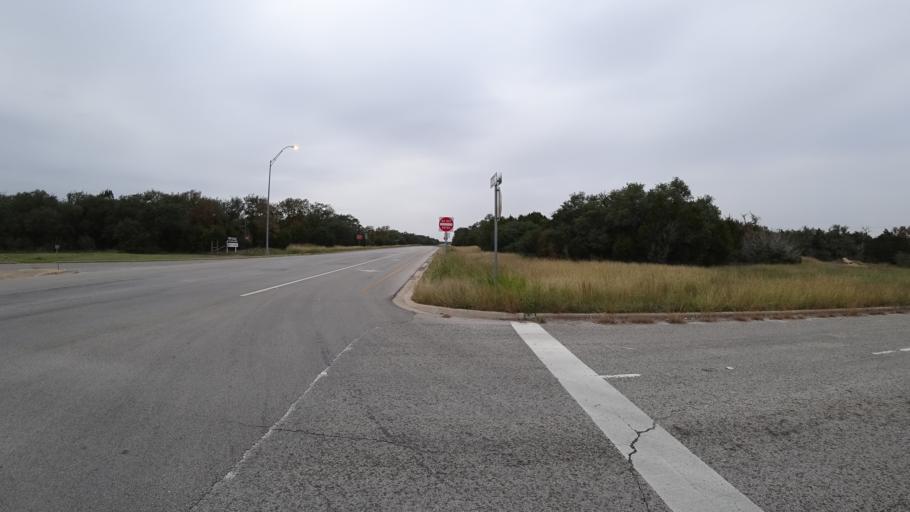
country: US
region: Texas
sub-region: Travis County
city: Shady Hollow
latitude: 30.1866
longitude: -97.9135
